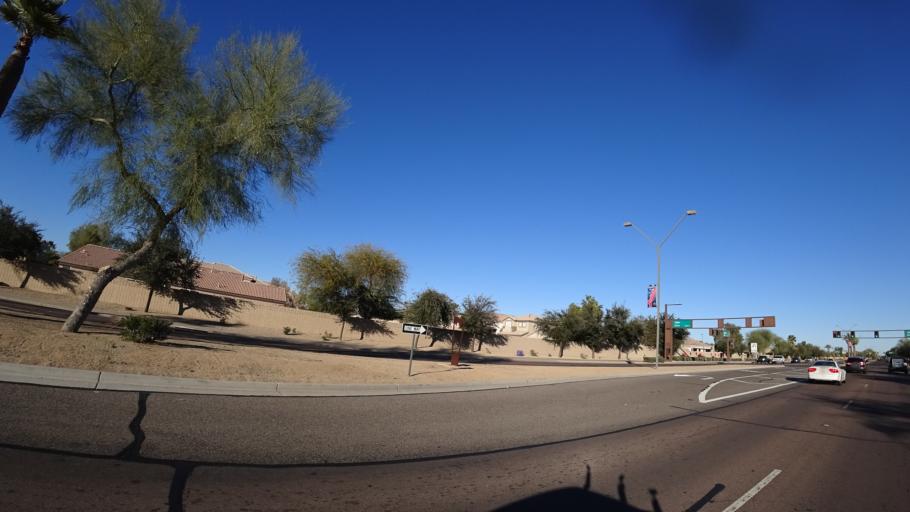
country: US
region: Arizona
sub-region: Maricopa County
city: Avondale
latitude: 33.4643
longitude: -112.3534
